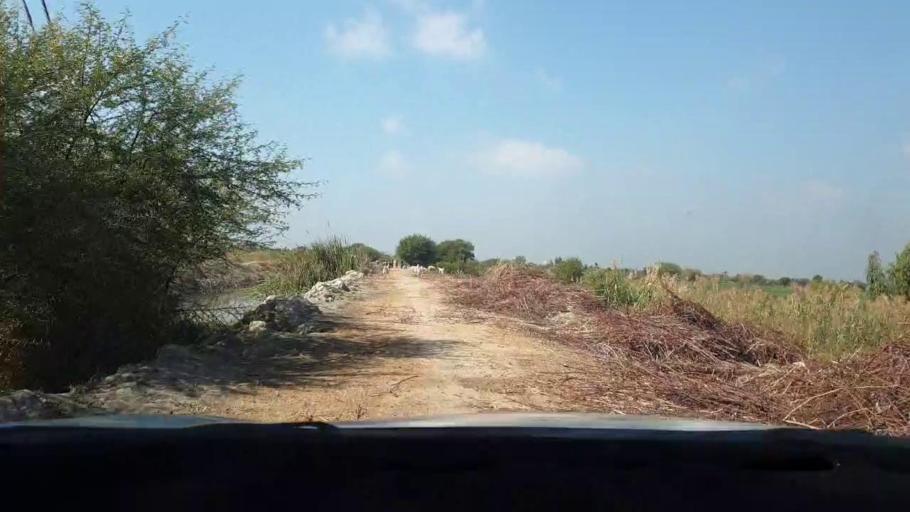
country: PK
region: Sindh
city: Berani
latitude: 25.7438
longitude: 68.9190
